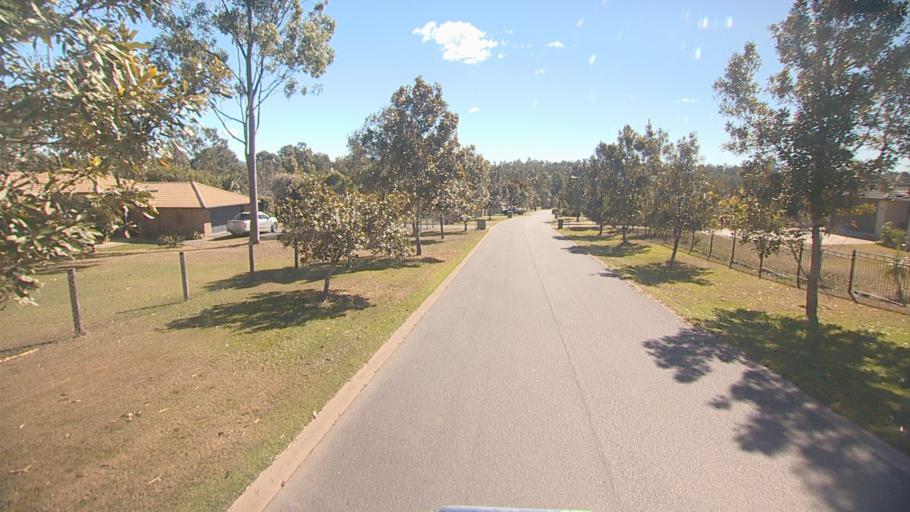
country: AU
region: Queensland
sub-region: Logan
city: North Maclean
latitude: -27.7574
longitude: 152.9538
